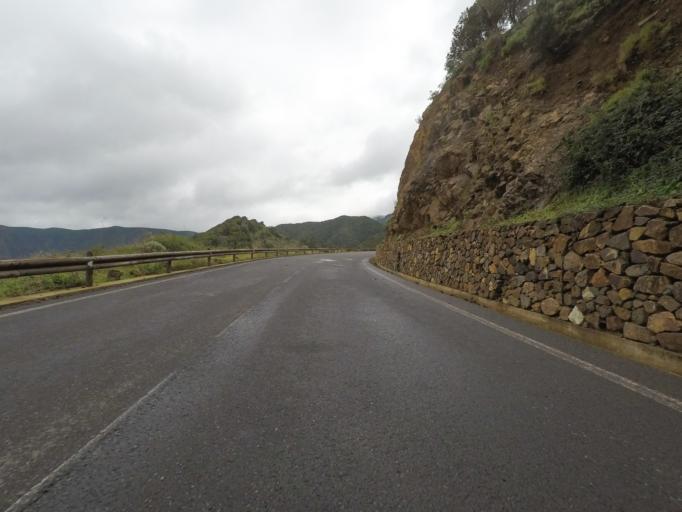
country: ES
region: Canary Islands
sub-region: Provincia de Santa Cruz de Tenerife
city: Vallehermosa
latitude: 28.1617
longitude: -17.2855
